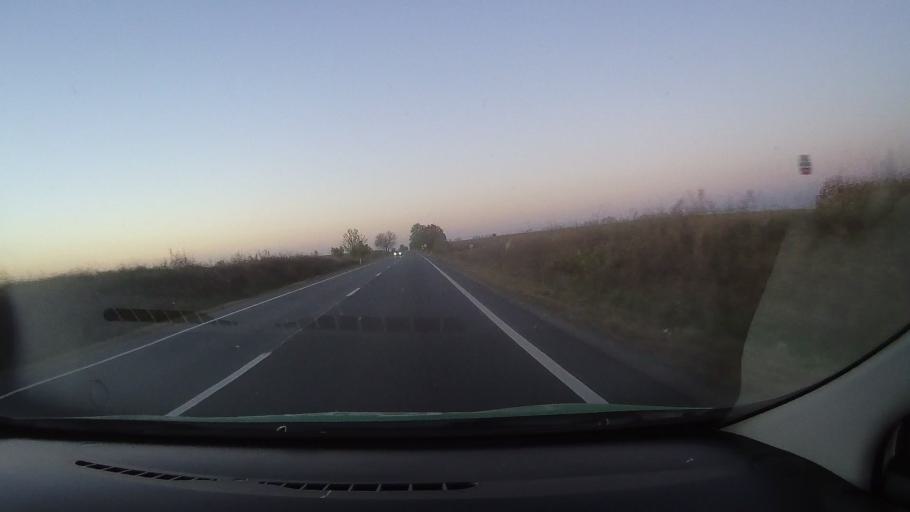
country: RO
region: Bihor
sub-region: Comuna Tarcea
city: Tarcea
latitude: 47.4701
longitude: 22.1653
